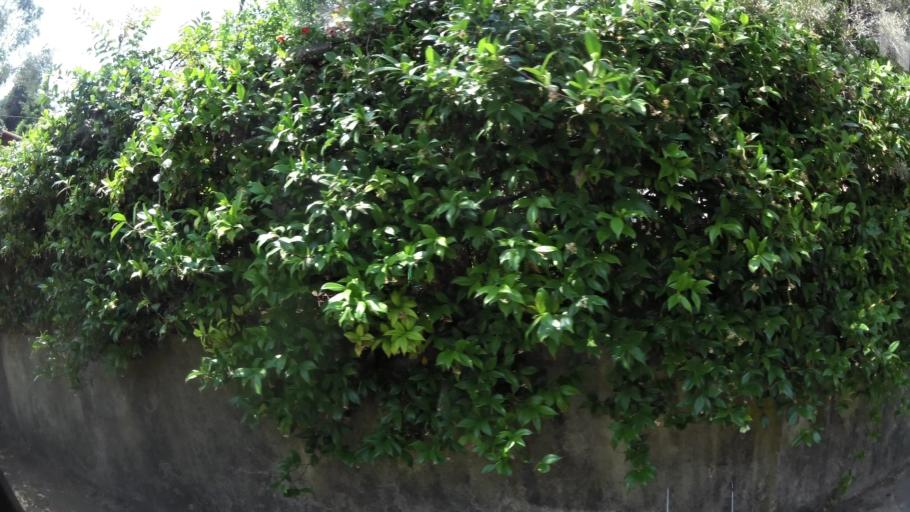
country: GR
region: Central Macedonia
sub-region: Nomos Imathias
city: Veroia
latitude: 40.5185
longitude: 22.1951
